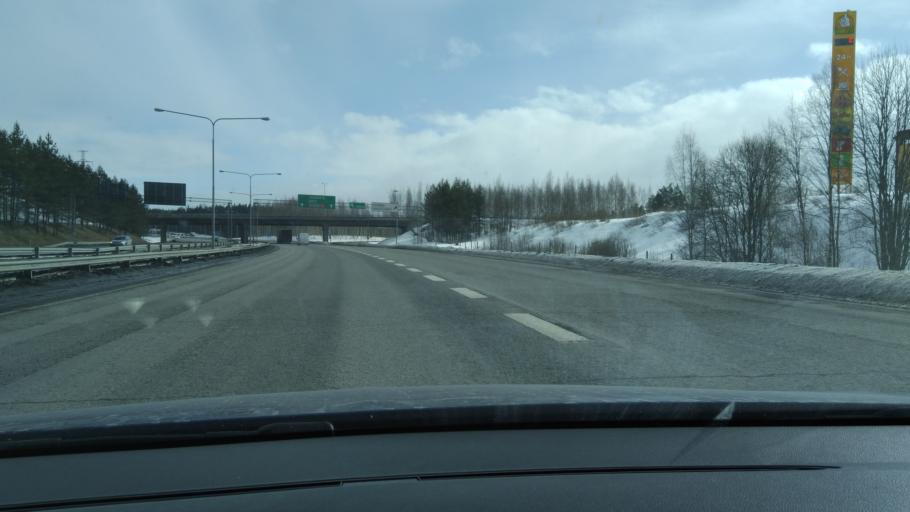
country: FI
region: Pirkanmaa
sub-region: Tampere
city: Tampere
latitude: 61.4604
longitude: 23.7873
